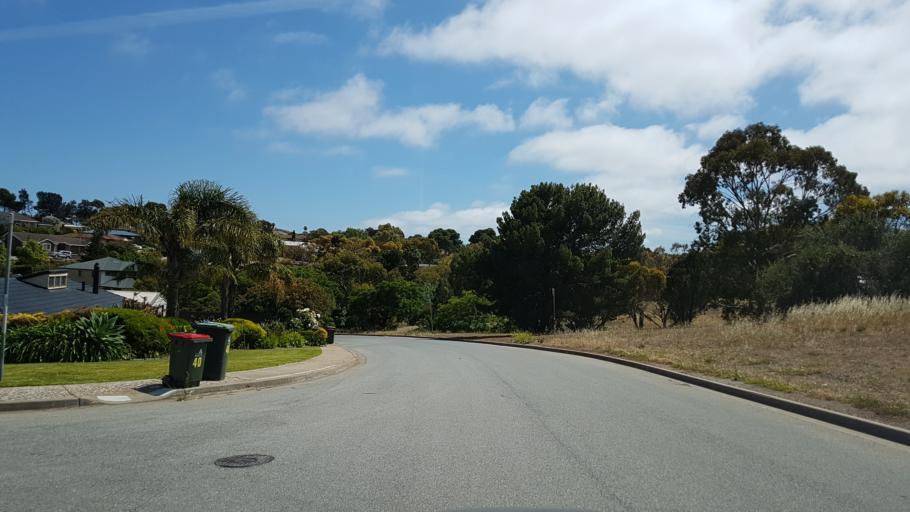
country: AU
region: South Australia
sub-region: Marion
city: Happy Valley
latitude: -35.0744
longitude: 138.5187
